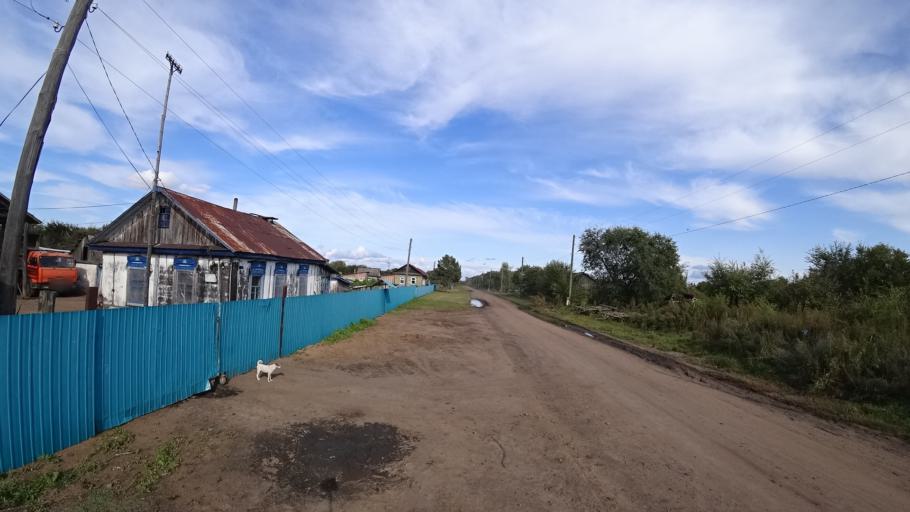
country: RU
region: Amur
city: Arkhara
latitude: 49.3515
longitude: 130.1030
